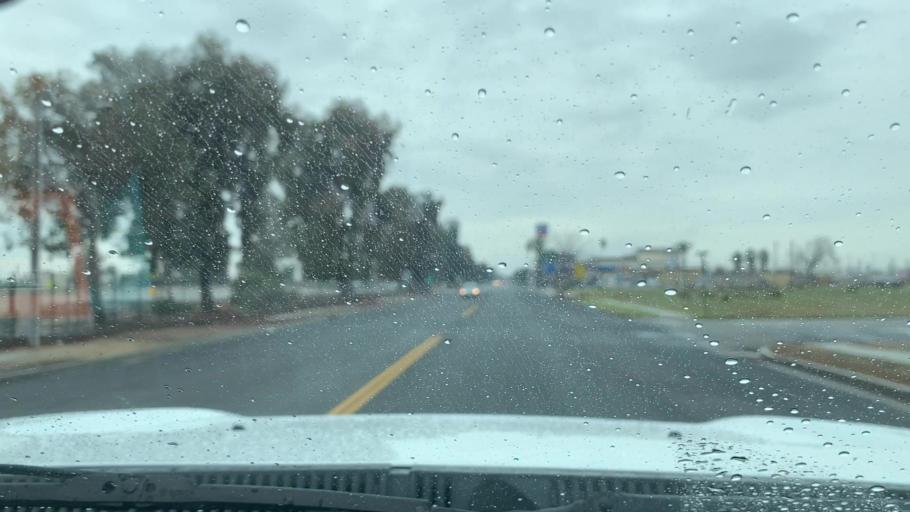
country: US
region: California
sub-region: Kern County
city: Delano
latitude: 35.7656
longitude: -119.2493
